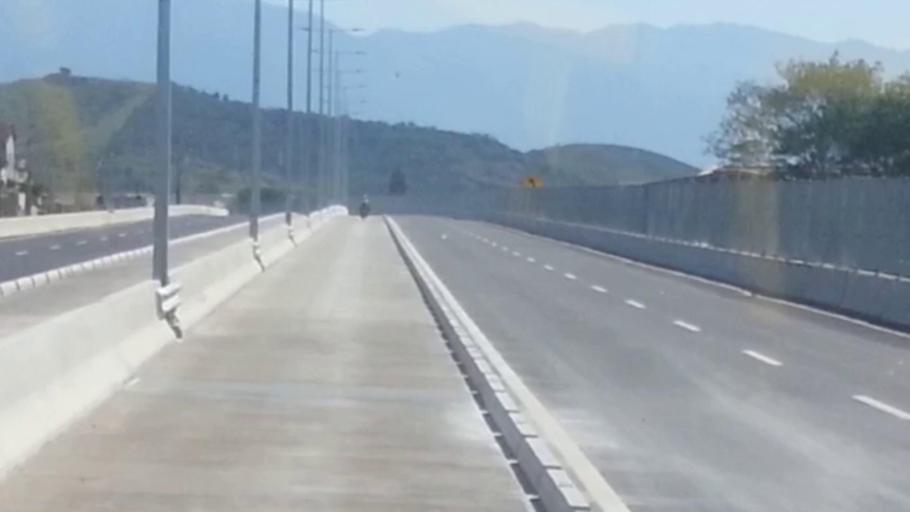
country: BR
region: Rio de Janeiro
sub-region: Nilopolis
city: Nilopolis
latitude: -22.8752
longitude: -43.4059
